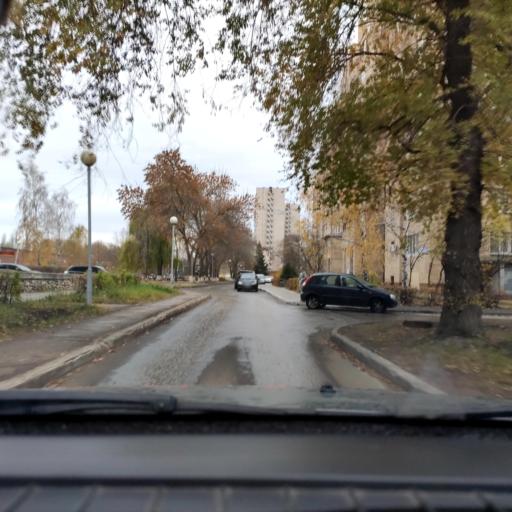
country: RU
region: Samara
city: Tol'yatti
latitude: 53.5118
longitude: 49.3027
